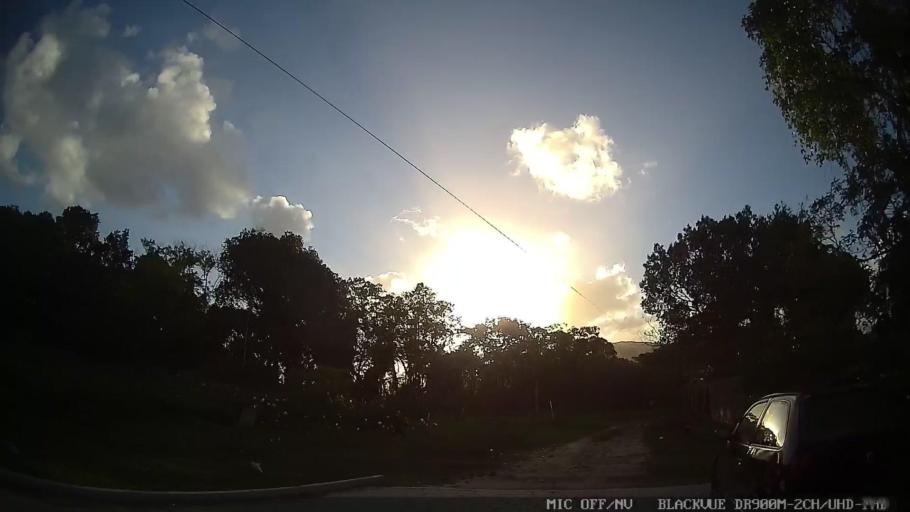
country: BR
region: Sao Paulo
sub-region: Itanhaem
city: Itanhaem
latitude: -24.1421
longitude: -46.7212
